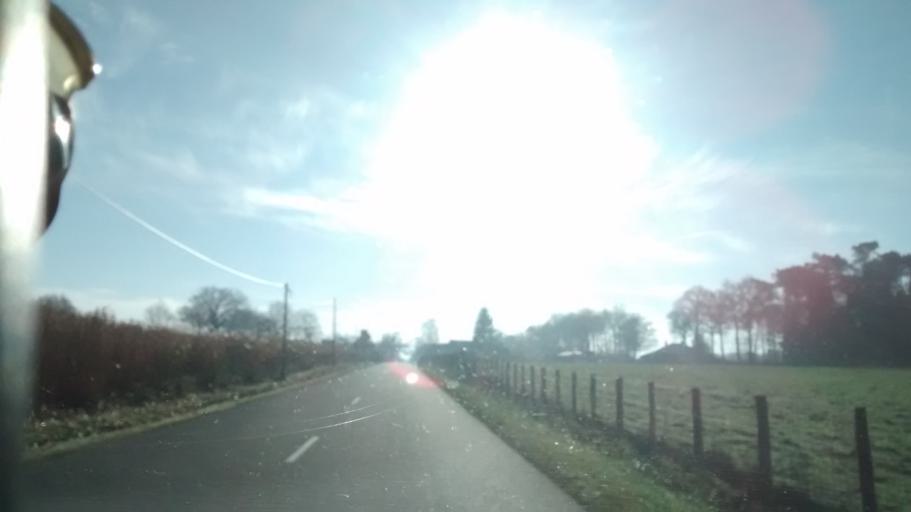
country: FR
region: Brittany
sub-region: Departement d'Ille-et-Vilaine
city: La Bouexiere
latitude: 48.1616
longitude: -1.4180
